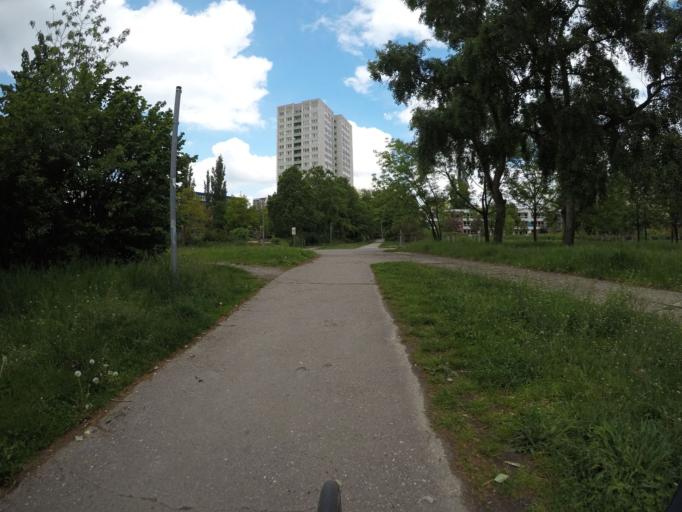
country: DE
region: Berlin
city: Marzahn
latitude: 52.5519
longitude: 13.5573
